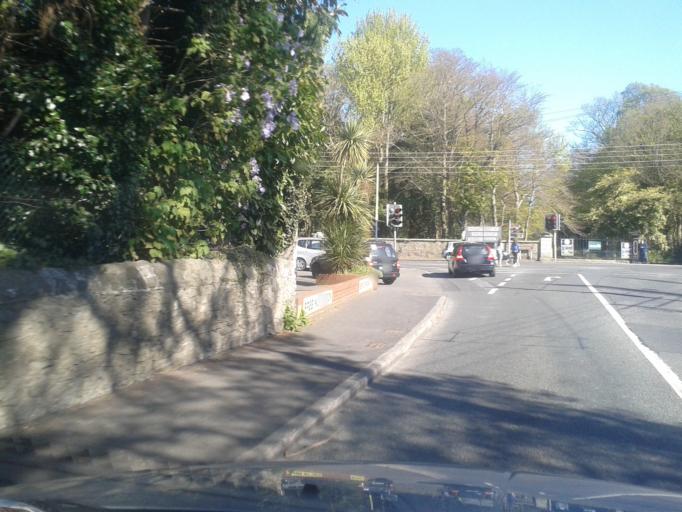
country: IE
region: Leinster
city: Malahide
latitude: 53.4461
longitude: -6.1734
